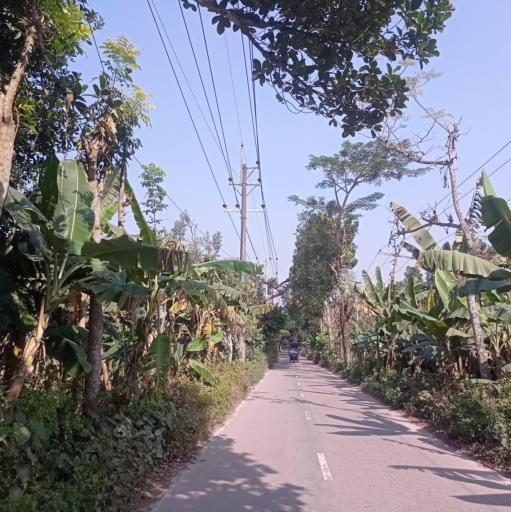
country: BD
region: Dhaka
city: Narsingdi
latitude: 24.0268
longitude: 90.6709
